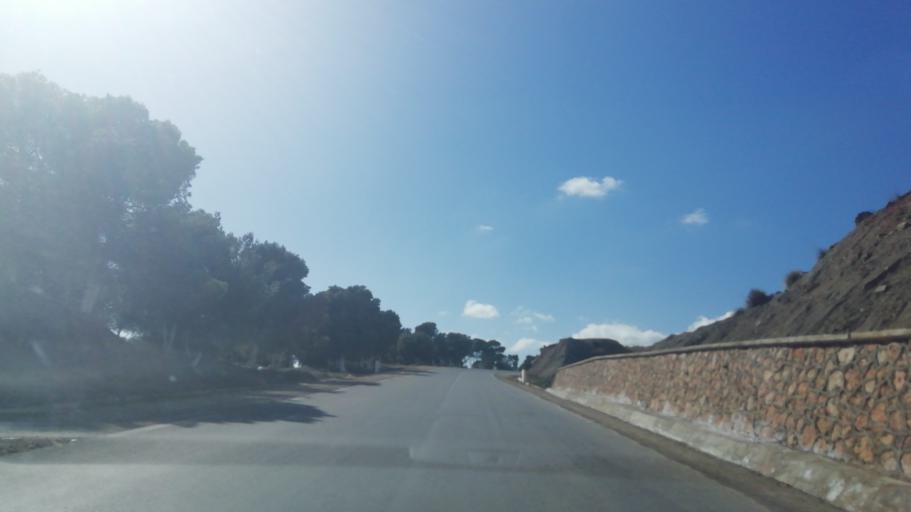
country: DZ
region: Relizane
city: Djidiouia
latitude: 36.0951
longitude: 0.5352
